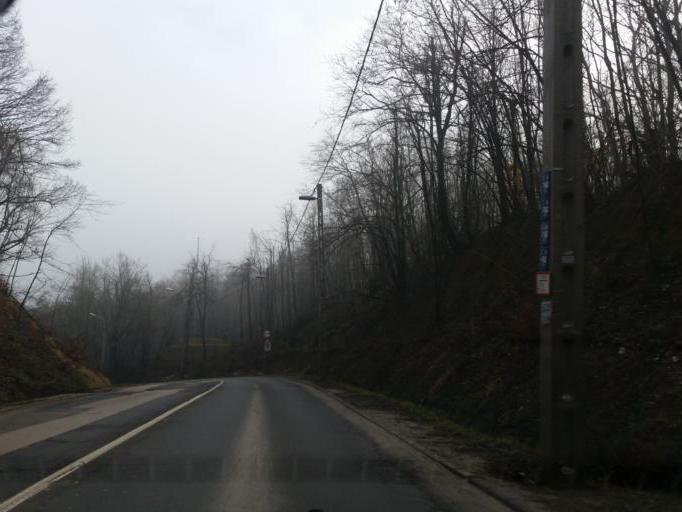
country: HU
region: Pest
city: Budakeszi
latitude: 47.5254
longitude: 18.9466
